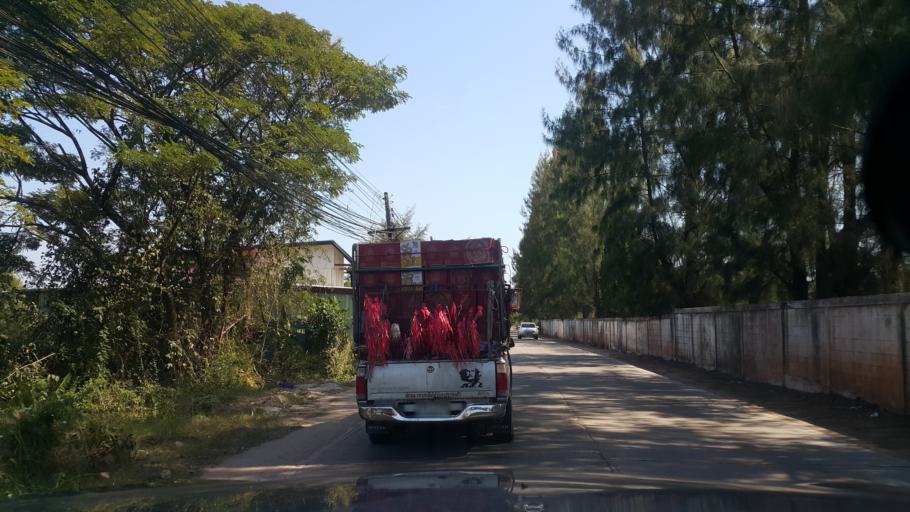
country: TH
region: Changwat Udon Thani
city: Udon Thani
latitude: 17.4543
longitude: 102.7820
